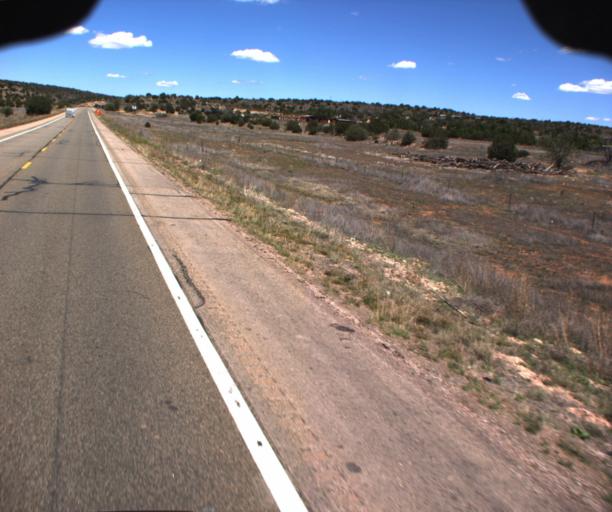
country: US
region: Arizona
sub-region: Yavapai County
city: Paulden
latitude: 34.9187
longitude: -112.4550
